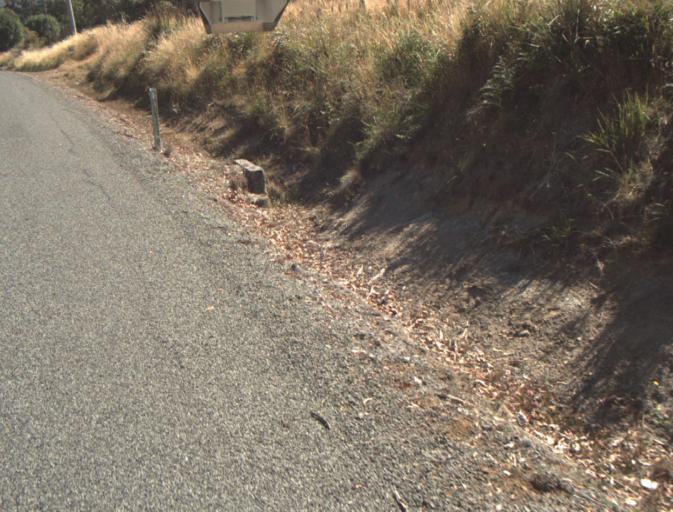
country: AU
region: Tasmania
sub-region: Launceston
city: Newstead
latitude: -41.3576
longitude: 147.3029
